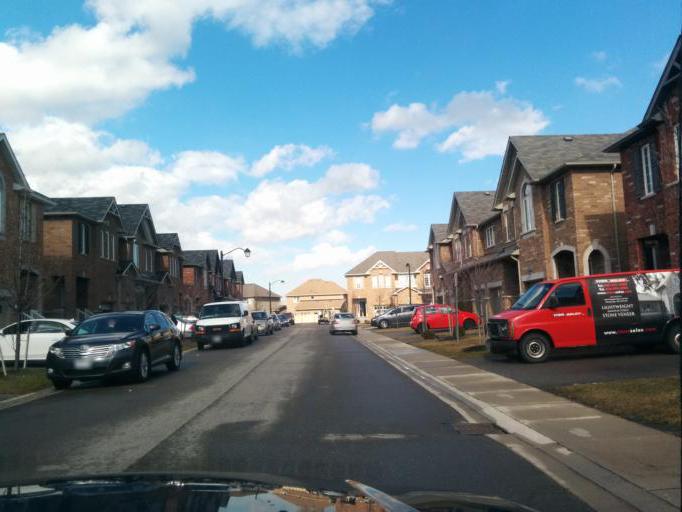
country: CA
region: Ontario
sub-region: Halton
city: Milton
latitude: 43.4992
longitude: -79.8665
